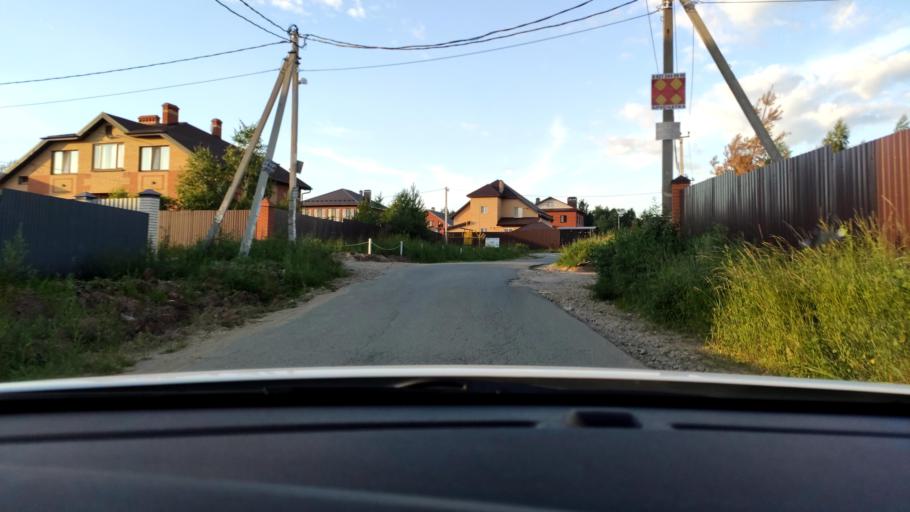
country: RU
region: Tatarstan
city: Stolbishchi
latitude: 55.7604
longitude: 49.2965
